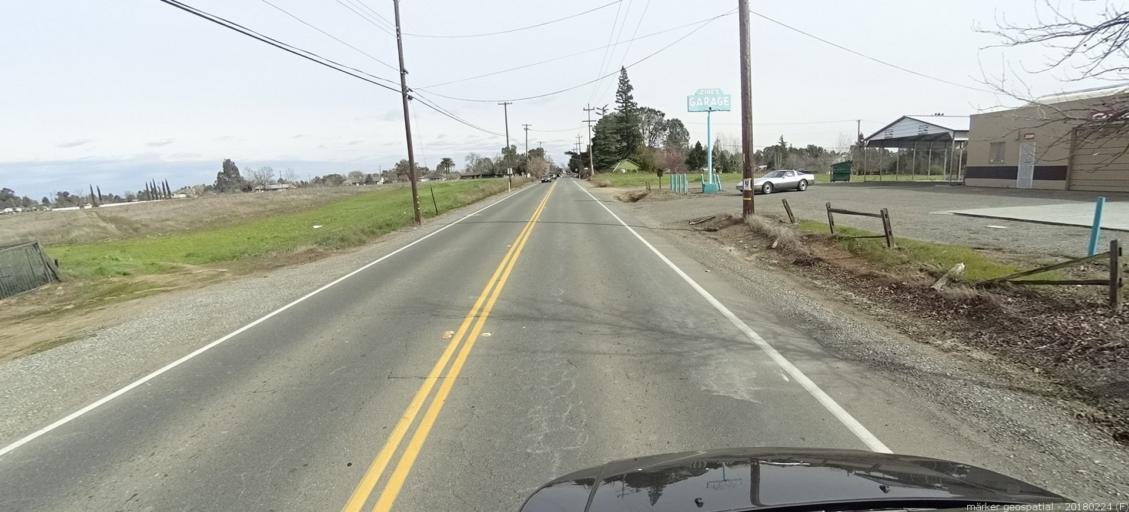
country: US
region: California
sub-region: Sacramento County
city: Elverta
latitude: 38.7145
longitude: -121.4607
